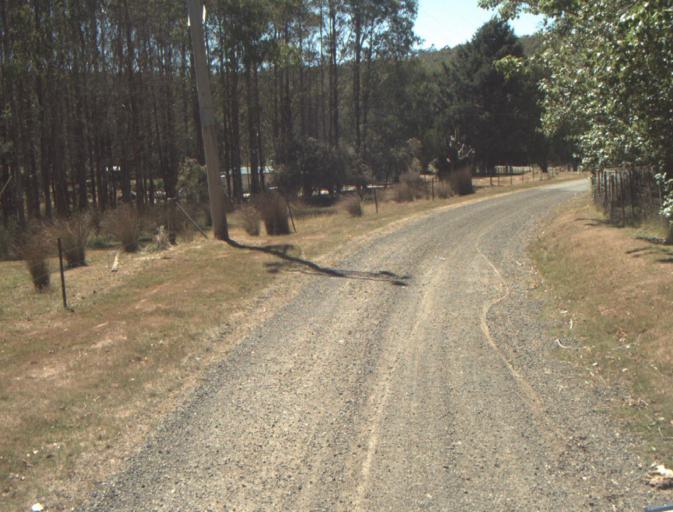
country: AU
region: Tasmania
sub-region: Dorset
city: Scottsdale
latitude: -41.2735
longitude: 147.3446
